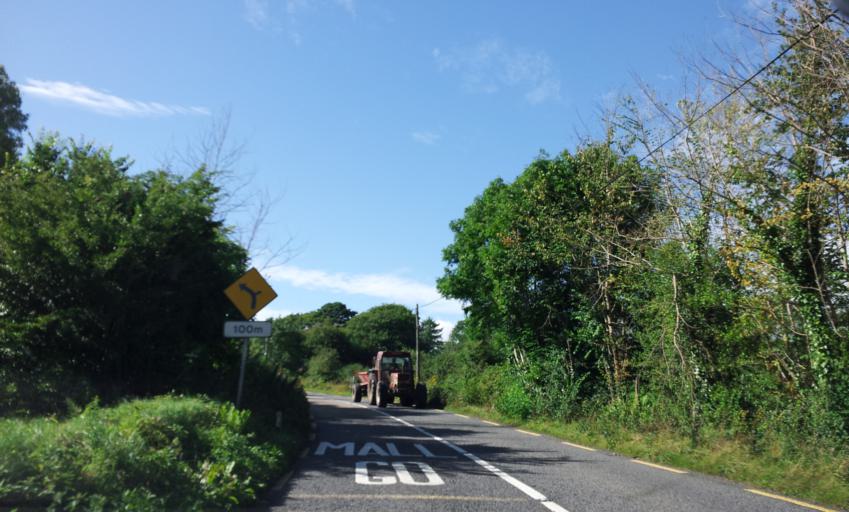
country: IE
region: Munster
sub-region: County Cork
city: Macroom
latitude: 51.9202
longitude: -9.0871
